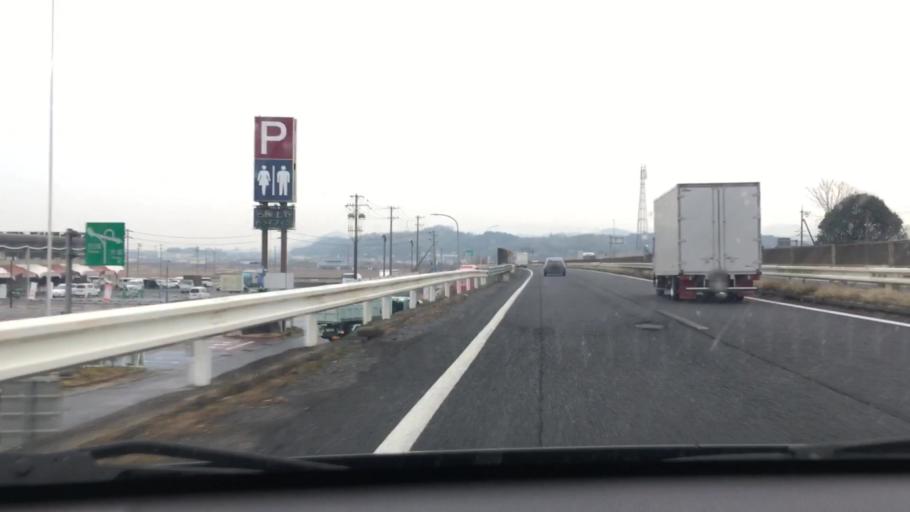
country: JP
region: Mie
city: Ueno-ebisumachi
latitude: 34.7389
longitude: 136.1105
